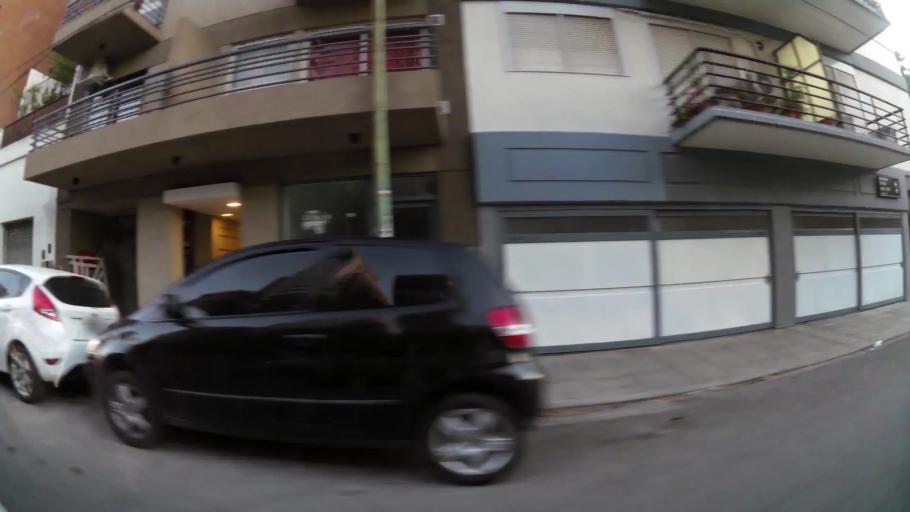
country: AR
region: Buenos Aires F.D.
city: Colegiales
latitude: -34.5492
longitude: -58.4717
